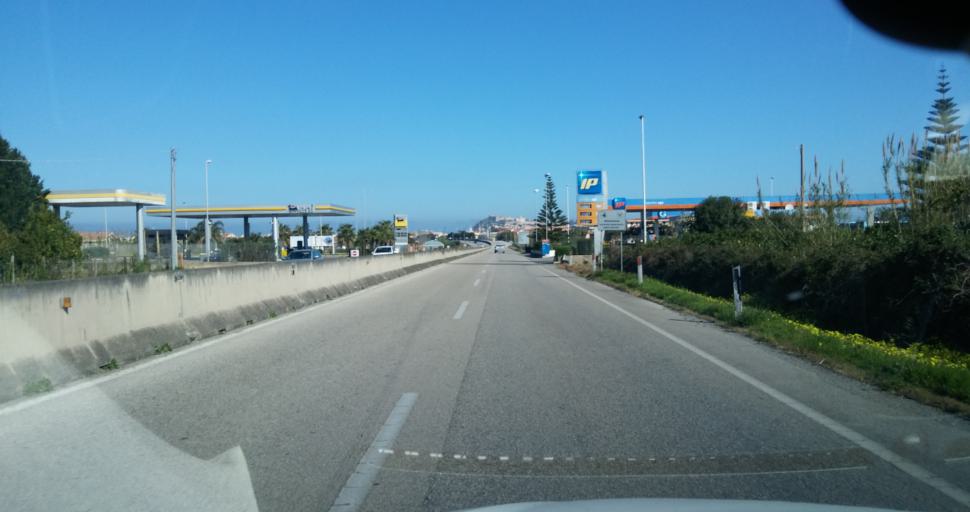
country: IT
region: Sicily
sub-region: Messina
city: Milazzo
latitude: 38.2003
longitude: 15.2470
